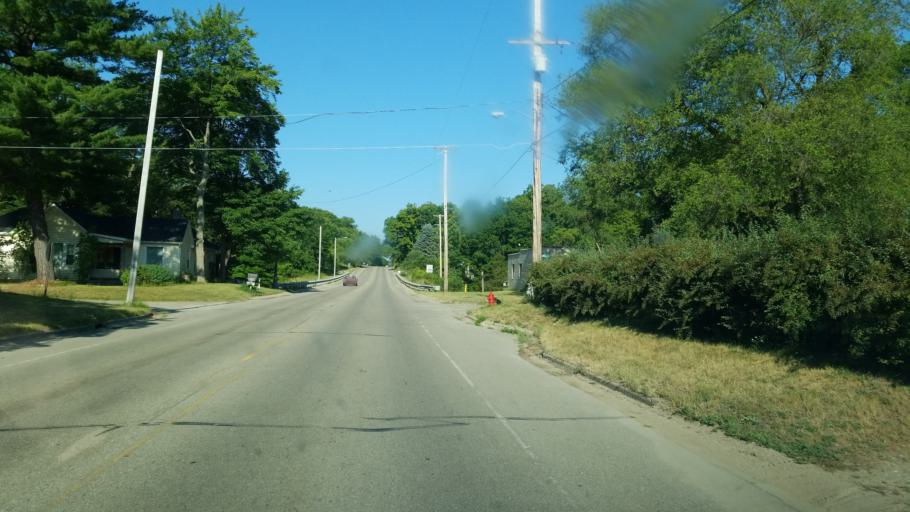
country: US
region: Michigan
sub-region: Montcalm County
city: Howard City
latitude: 43.4896
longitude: -85.4471
